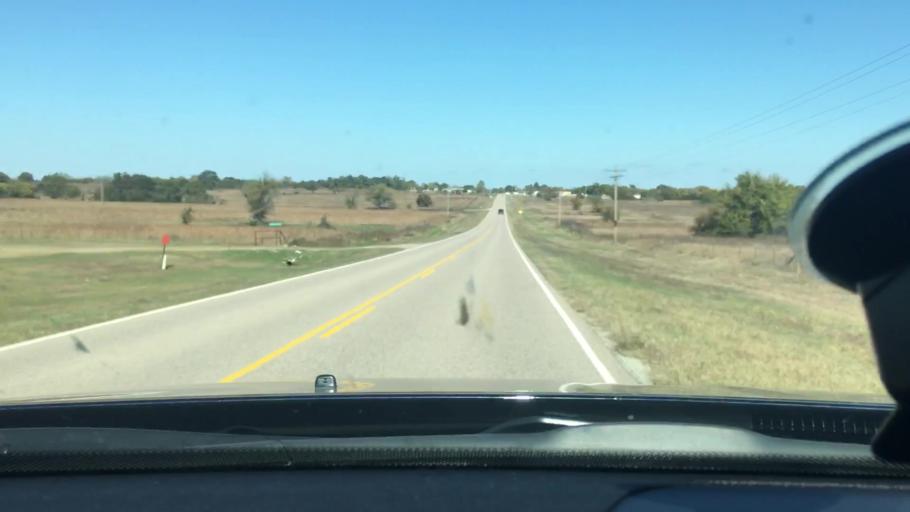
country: US
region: Oklahoma
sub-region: Johnston County
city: Tishomingo
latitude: 34.4336
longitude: -96.6360
